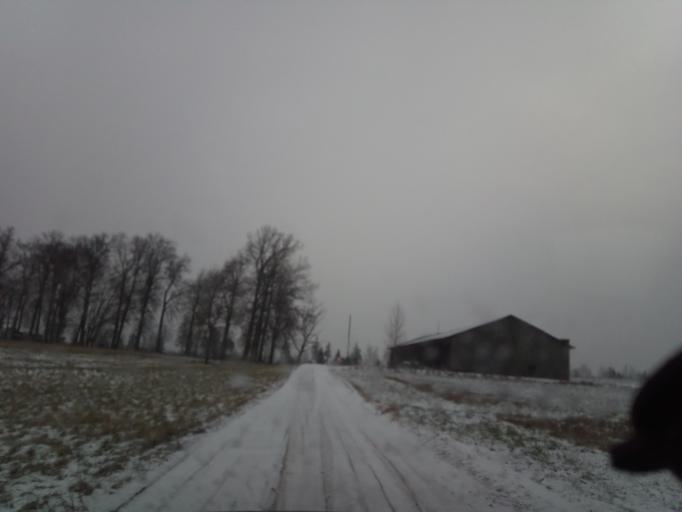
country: LT
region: Utenos apskritis
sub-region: Anyksciai
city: Anyksciai
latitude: 55.4038
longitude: 25.1700
